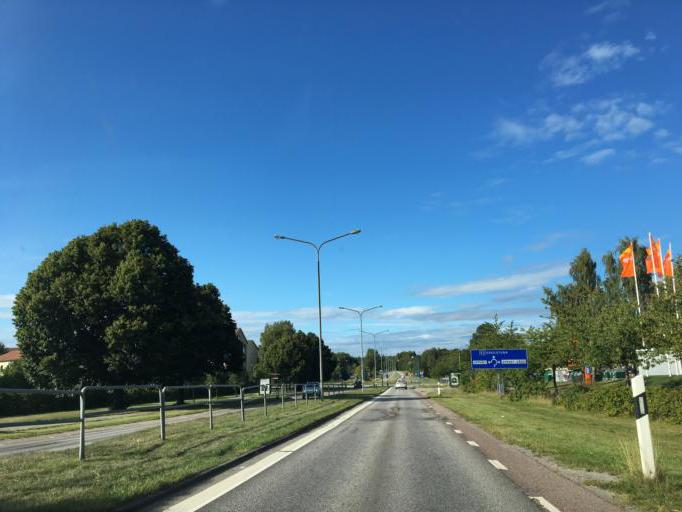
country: SE
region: Soedermanland
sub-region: Nykopings Kommun
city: Nykoping
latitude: 58.7689
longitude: 16.9868
